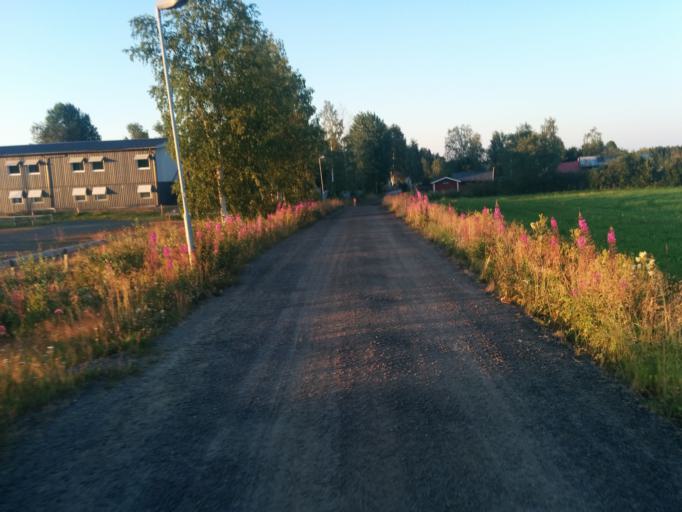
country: SE
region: Vaesterbotten
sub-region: Umea Kommun
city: Ersmark
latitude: 63.8537
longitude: 20.3827
